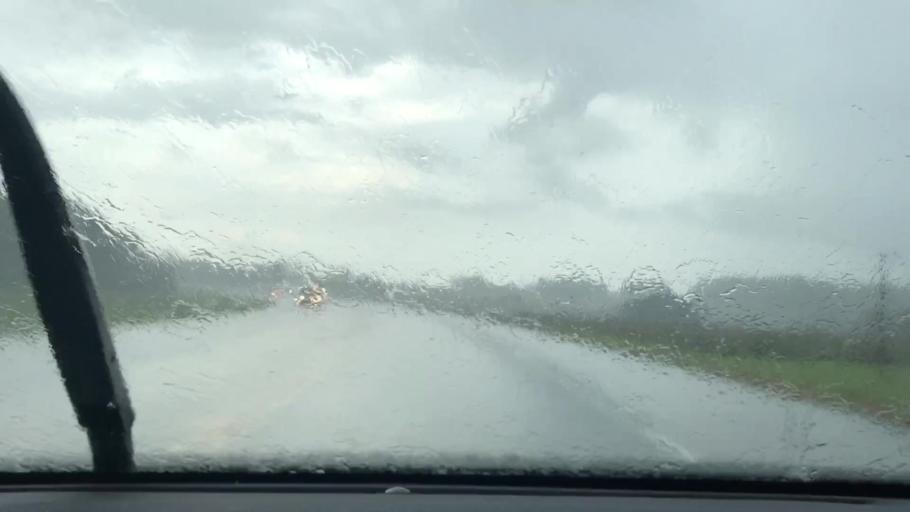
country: US
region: Tennessee
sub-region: Macon County
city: Lafayette
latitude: 36.4980
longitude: -85.9688
